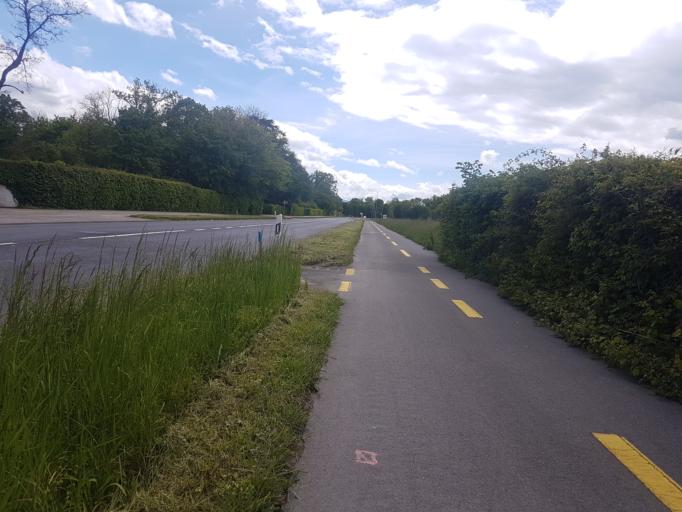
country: CH
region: Vaud
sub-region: Nyon District
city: Founex
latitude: 46.3447
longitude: 6.2059
